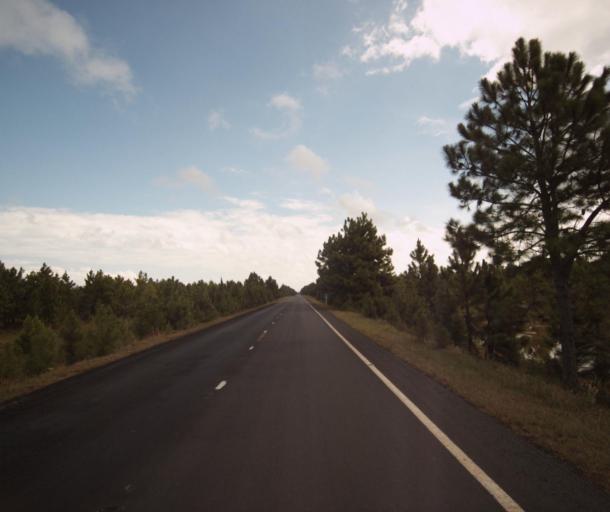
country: BR
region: Rio Grande do Sul
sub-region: Tapes
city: Tapes
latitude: -31.4253
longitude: -51.1836
